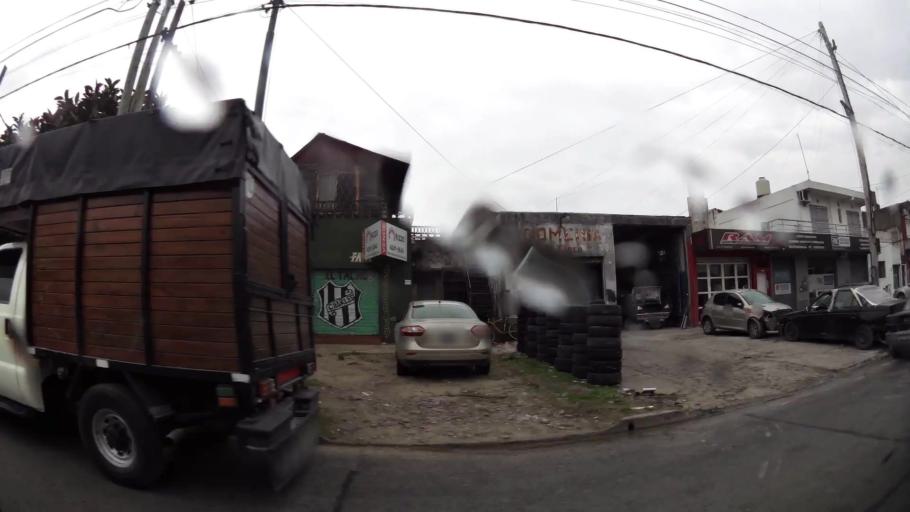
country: AR
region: Buenos Aires
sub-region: Partido de Lanus
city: Lanus
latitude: -34.6879
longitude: -58.3999
